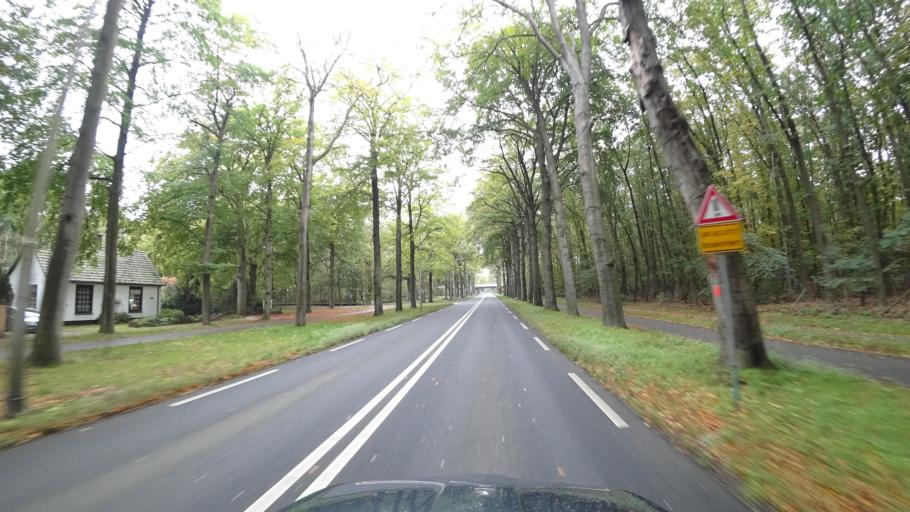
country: NL
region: North Holland
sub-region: Gemeente Hilversum
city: Hilversum
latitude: 52.2082
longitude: 5.2118
